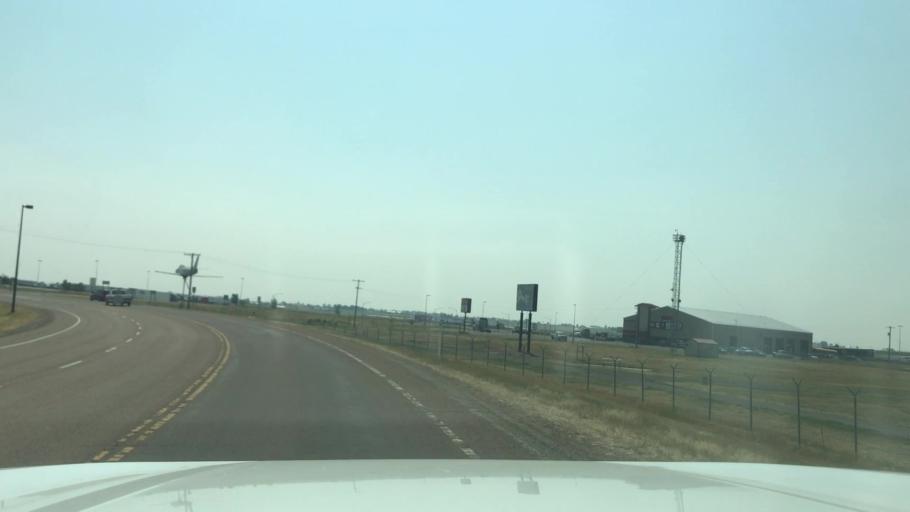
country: US
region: Montana
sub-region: Cascade County
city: Great Falls
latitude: 47.4745
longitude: -111.3623
